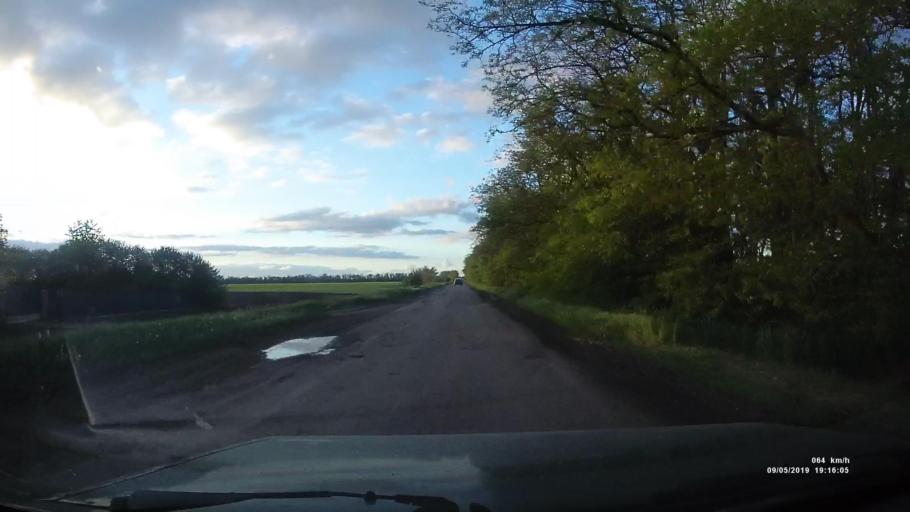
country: RU
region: Krasnodarskiy
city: Kanelovskaya
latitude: 46.7747
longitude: 39.2115
